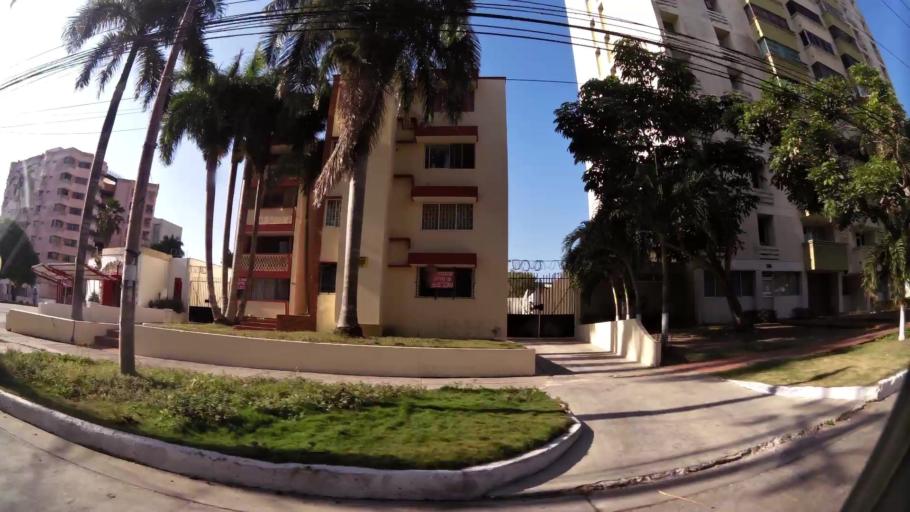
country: CO
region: Atlantico
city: Barranquilla
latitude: 10.9983
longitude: -74.7976
